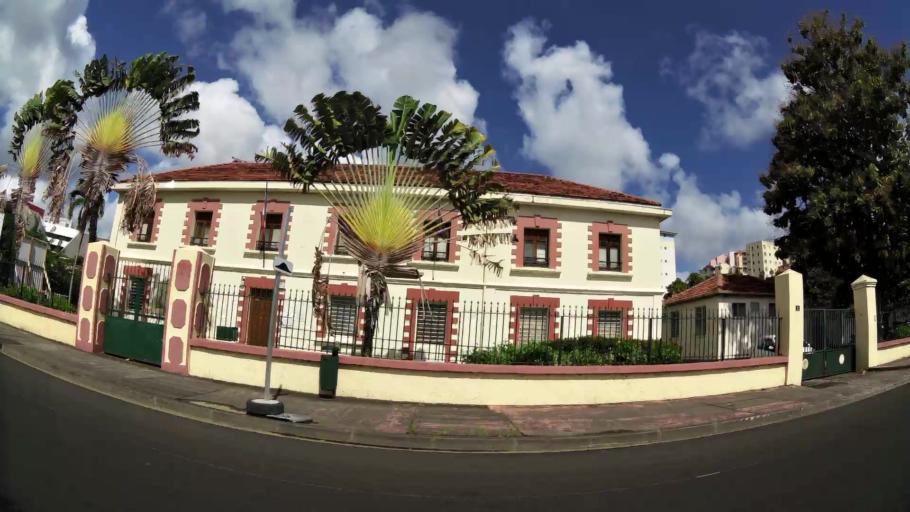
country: MQ
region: Martinique
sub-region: Martinique
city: Fort-de-France
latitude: 14.6052
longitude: -61.0641
